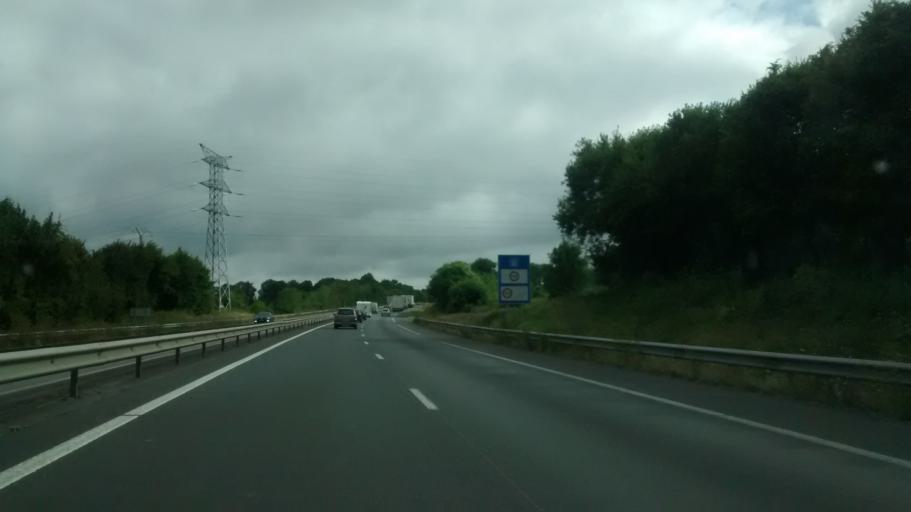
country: FR
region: Lower Normandy
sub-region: Departement du Calvados
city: Villers-Bocage
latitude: 49.0897
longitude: -0.6341
